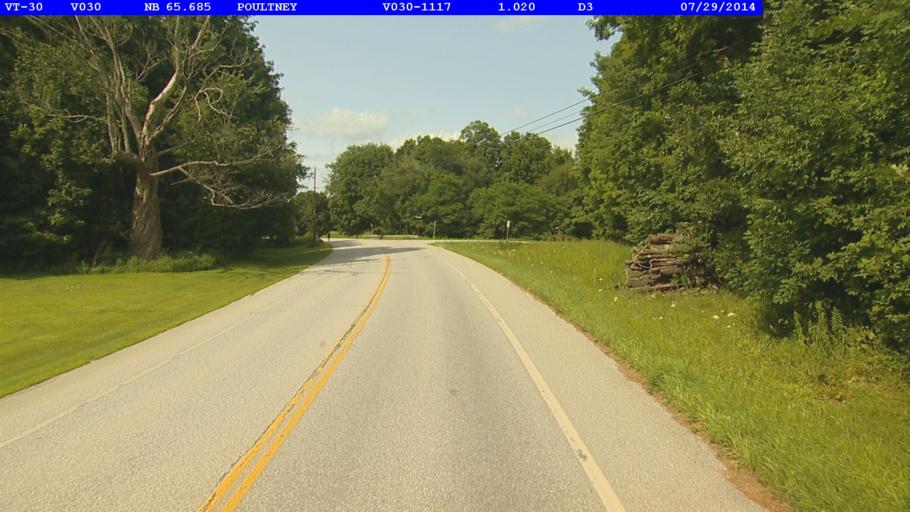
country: US
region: Vermont
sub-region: Rutland County
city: Poultney
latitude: 43.4783
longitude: -73.2009
